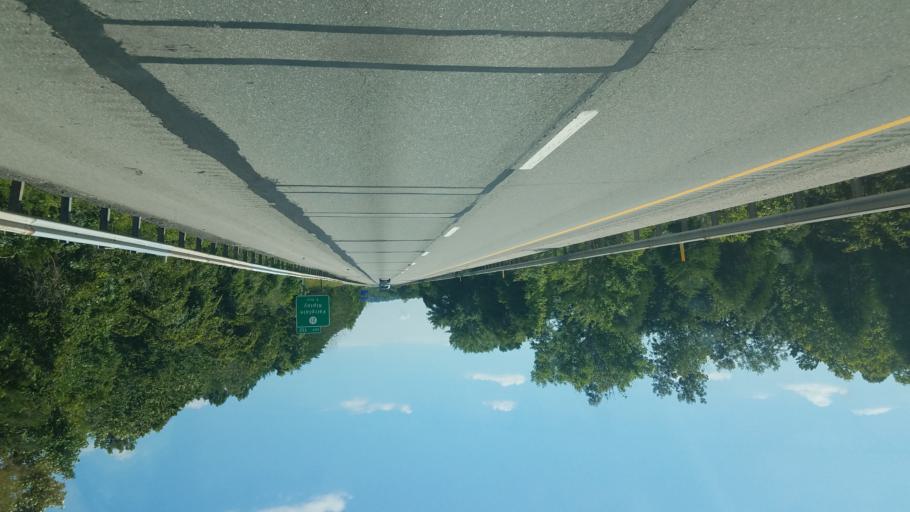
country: US
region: West Virginia
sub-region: Jackson County
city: Ripley
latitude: 38.7441
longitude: -81.6774
